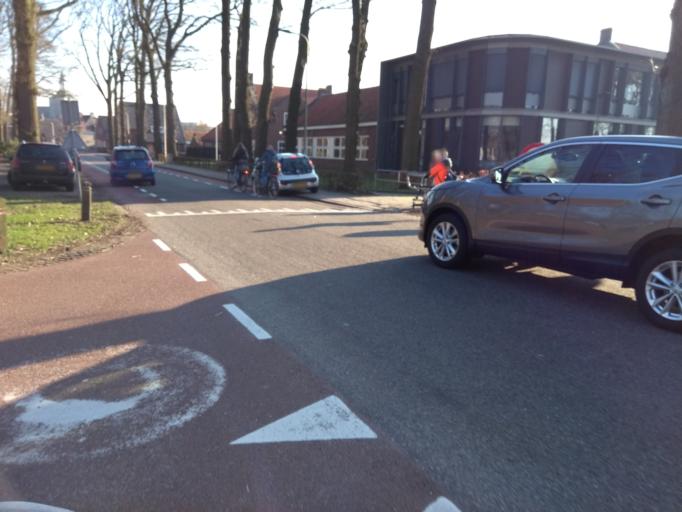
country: NL
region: Overijssel
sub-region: Gemeente Tubbergen
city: Tubbergen
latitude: 52.4104
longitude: 6.7785
